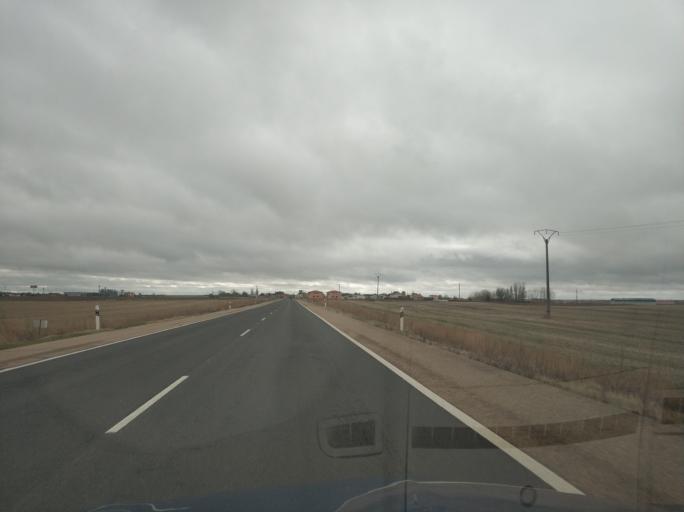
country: ES
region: Castille and Leon
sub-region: Provincia de Salamanca
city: Pedrosillo el Ralo
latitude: 41.0670
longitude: -5.5395
